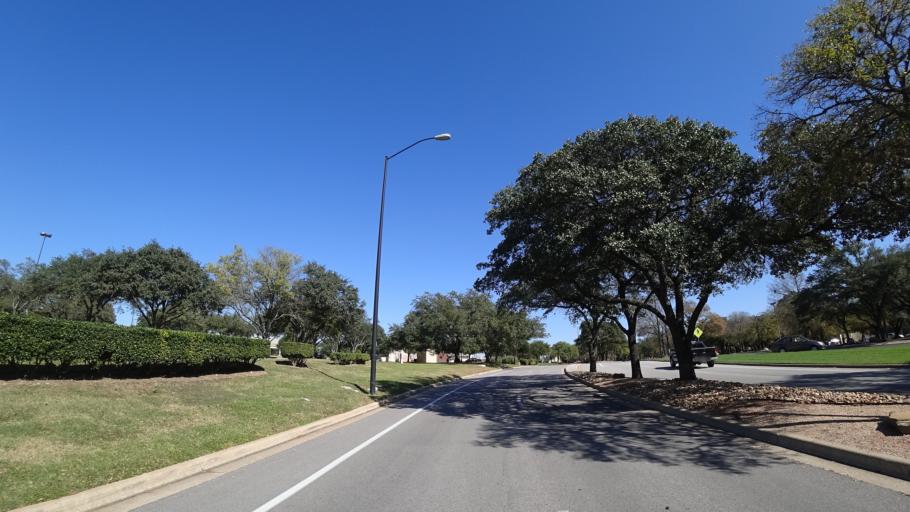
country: US
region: Texas
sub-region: Williamson County
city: Jollyville
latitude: 30.3928
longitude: -97.7515
